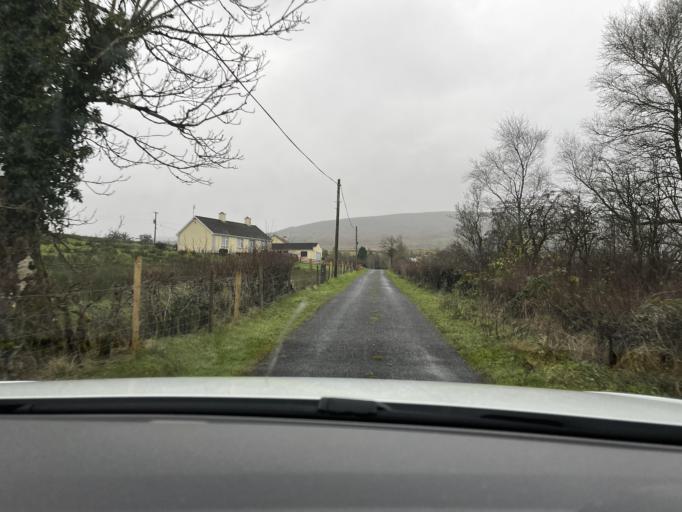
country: IE
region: Connaught
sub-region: County Leitrim
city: Manorhamilton
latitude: 54.2894
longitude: -8.0845
